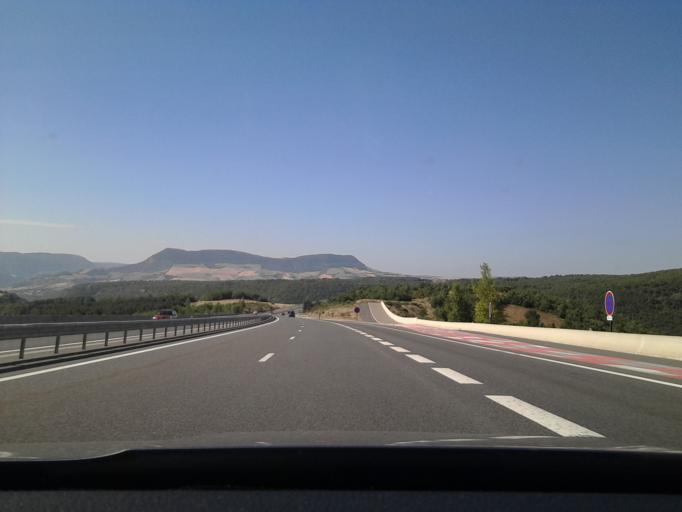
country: FR
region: Midi-Pyrenees
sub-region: Departement de l'Aveyron
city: Millau
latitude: 44.2071
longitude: 3.0676
